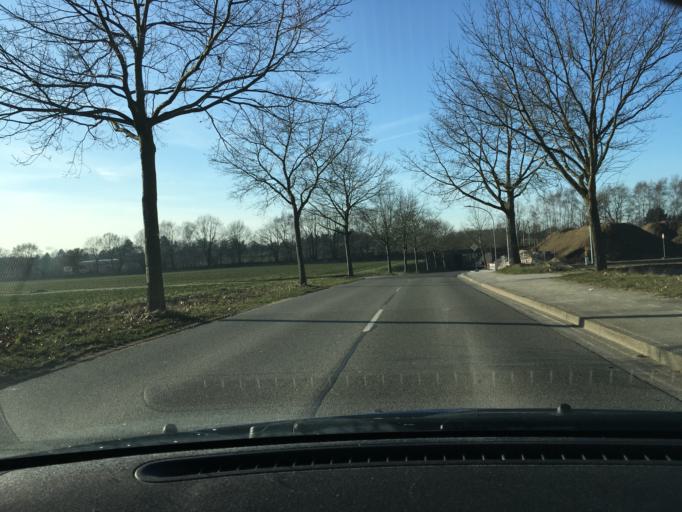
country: DE
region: Lower Saxony
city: Seevetal
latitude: 53.4001
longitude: 9.9743
